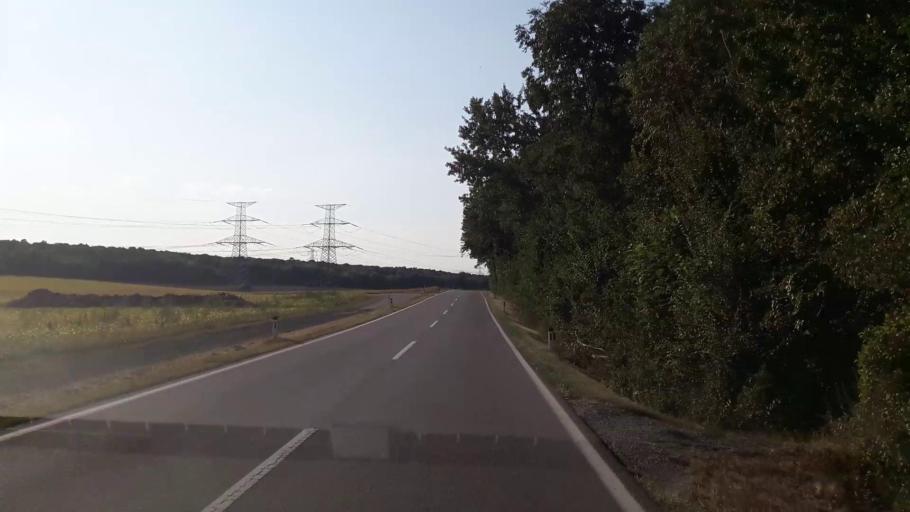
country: AT
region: Lower Austria
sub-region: Politischer Bezirk Ganserndorf
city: Orth an der Donau
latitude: 48.0771
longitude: 16.6852
